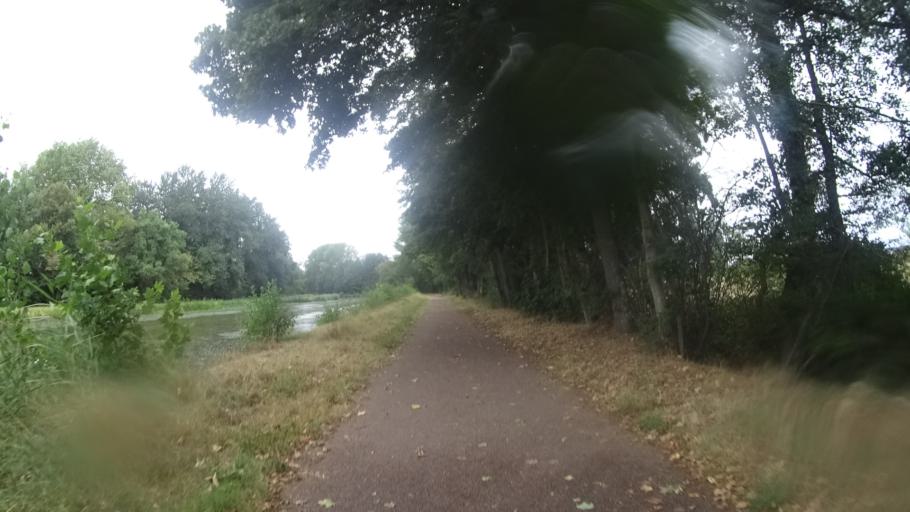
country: FR
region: Bourgogne
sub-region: Departement de la Nievre
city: Decize
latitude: 46.8193
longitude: 3.4493
